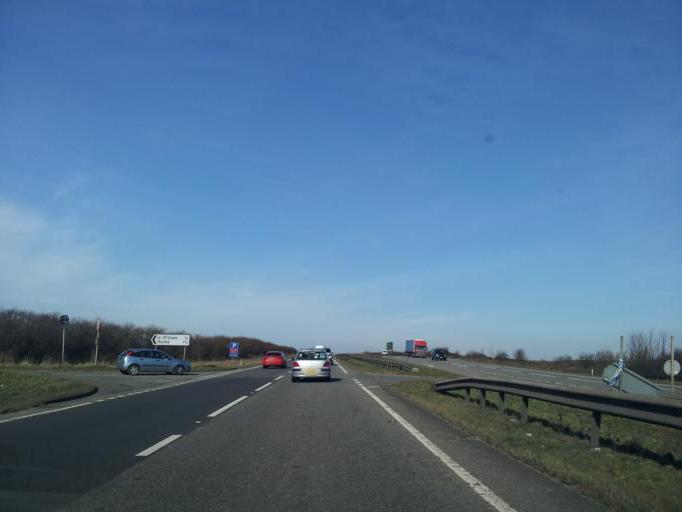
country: GB
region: England
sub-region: District of Rutland
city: Greetham
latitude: 52.7817
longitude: -0.6111
